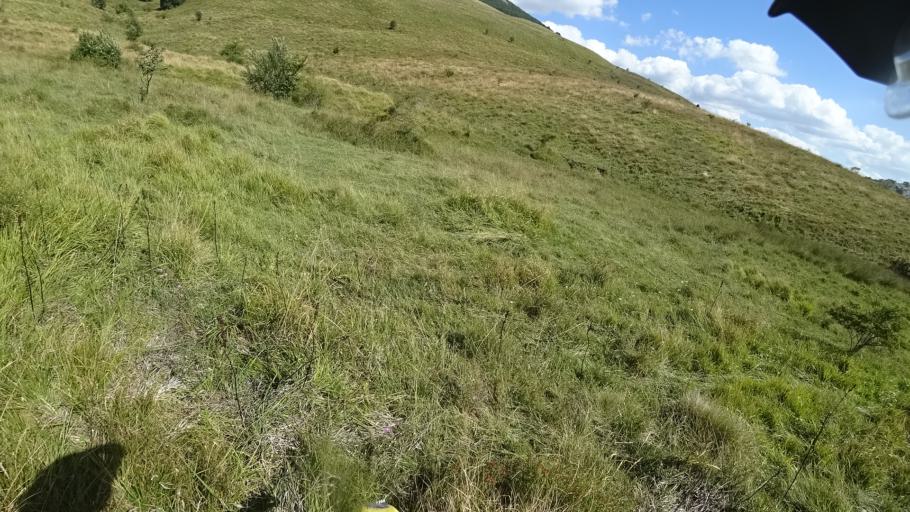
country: HR
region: Zadarska
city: Gracac
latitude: 44.4123
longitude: 16.0014
